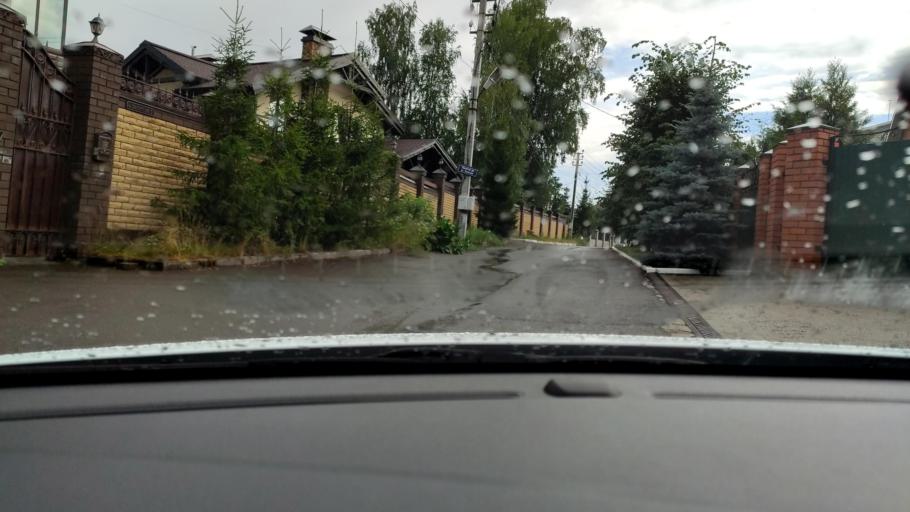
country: RU
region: Tatarstan
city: Stolbishchi
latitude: 55.7352
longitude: 49.2462
